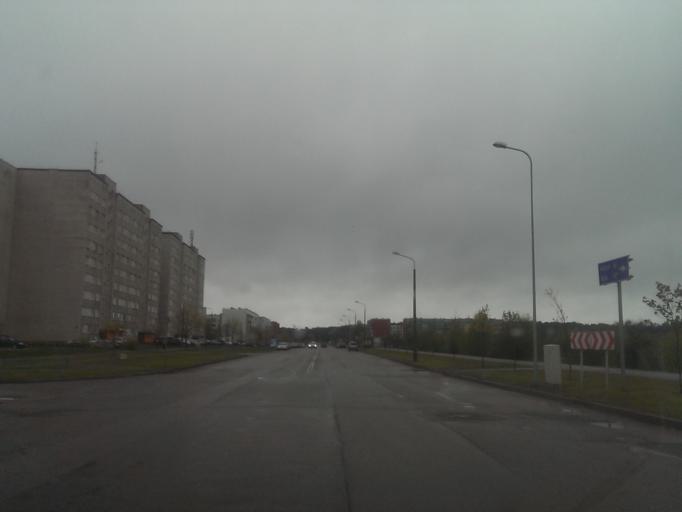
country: LV
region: Ventspils
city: Ventspils
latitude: 57.4063
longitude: 21.6035
